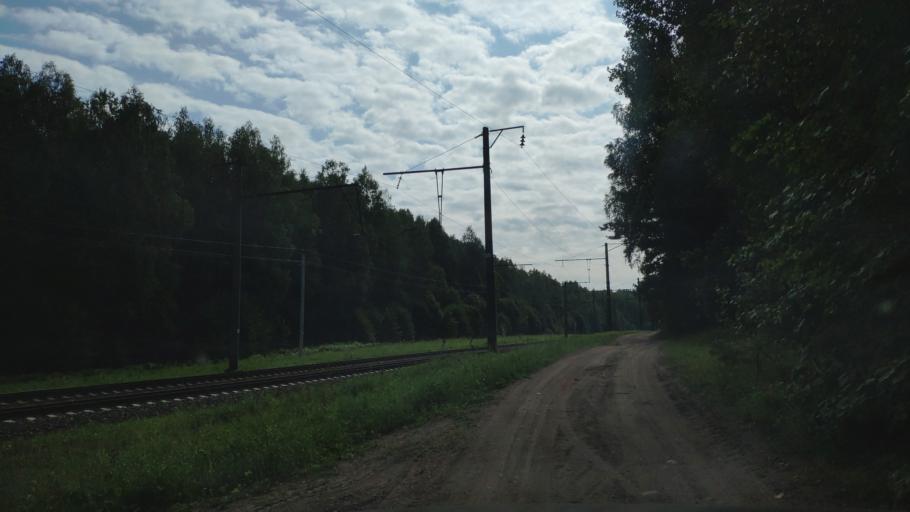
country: BY
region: Minsk
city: Khatsyezhyna
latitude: 53.9622
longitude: 27.3027
